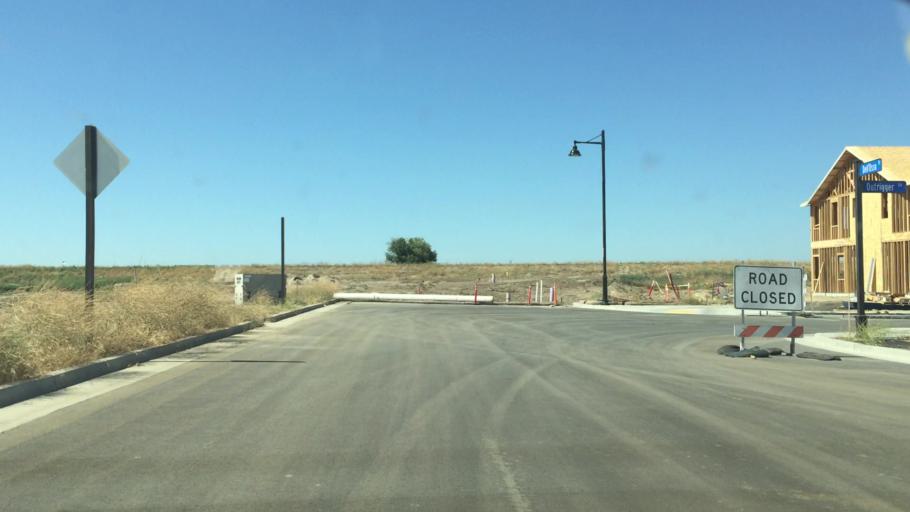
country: US
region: California
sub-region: San Joaquin County
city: Lathrop
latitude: 37.8052
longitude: -121.3301
